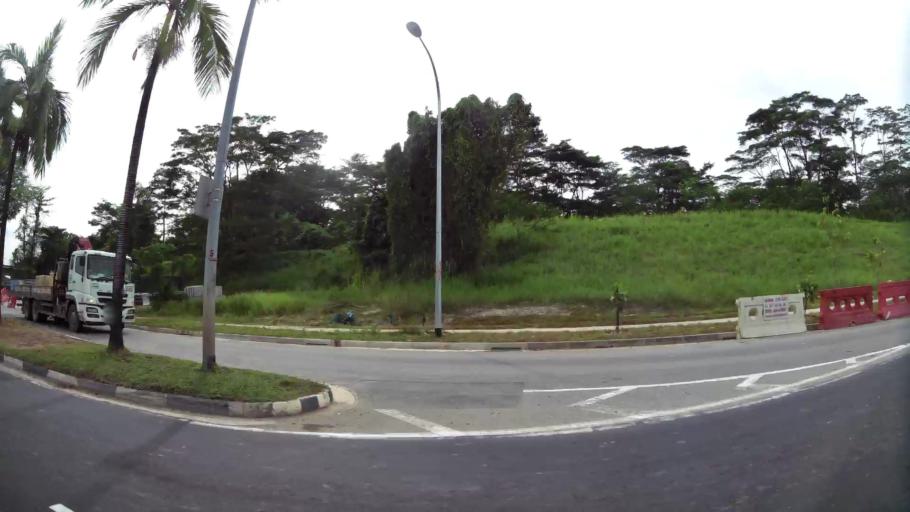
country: MY
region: Johor
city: Johor Bahru
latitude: 1.4243
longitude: 103.7569
